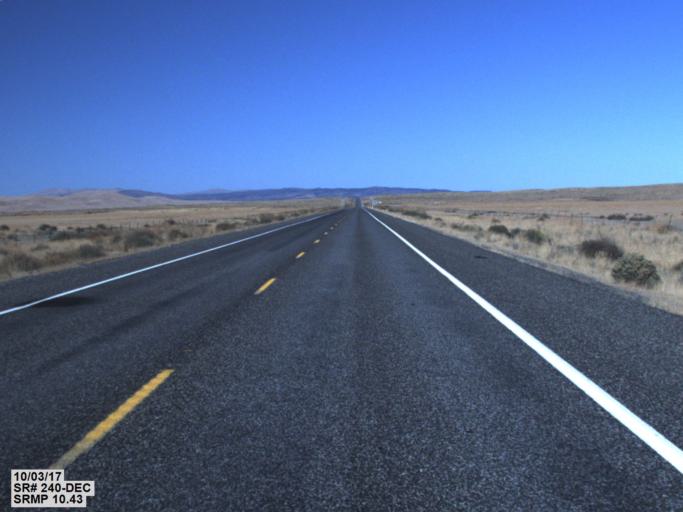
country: US
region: Washington
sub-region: Benton County
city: Benton City
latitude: 46.4821
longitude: -119.5736
